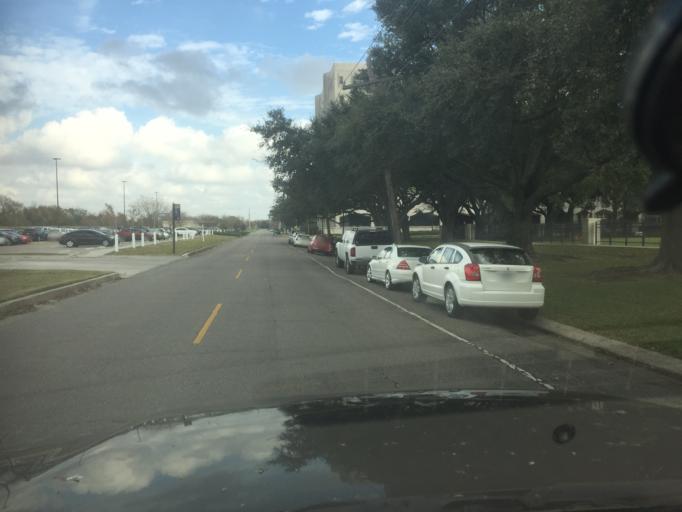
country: US
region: Louisiana
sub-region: Orleans Parish
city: New Orleans
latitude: 29.9918
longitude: -90.0854
